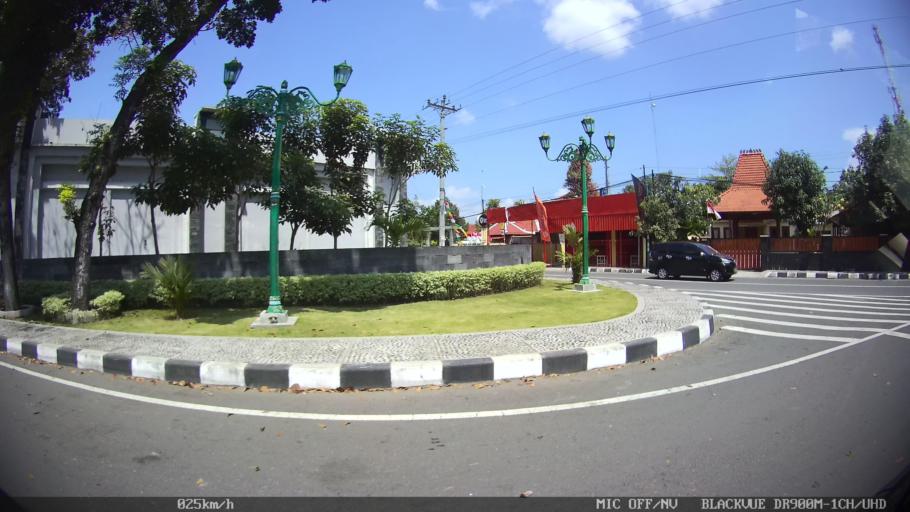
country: ID
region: Daerah Istimewa Yogyakarta
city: Pundong
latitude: -7.9201
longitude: 110.3815
